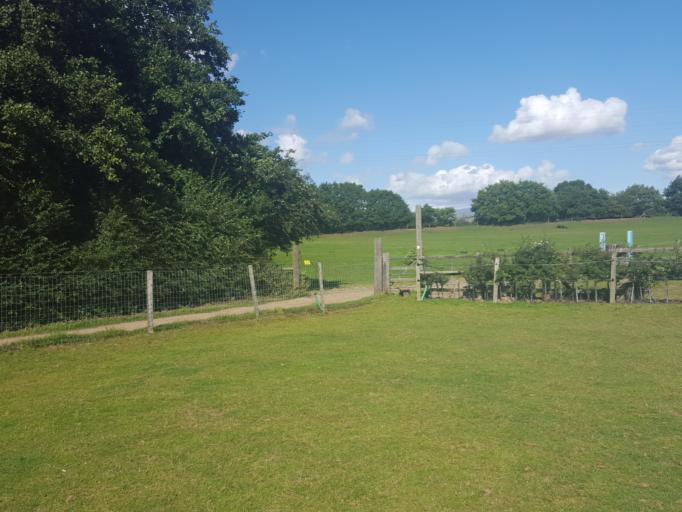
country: GB
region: England
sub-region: Essex
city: Alresford
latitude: 51.8508
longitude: 1.0196
